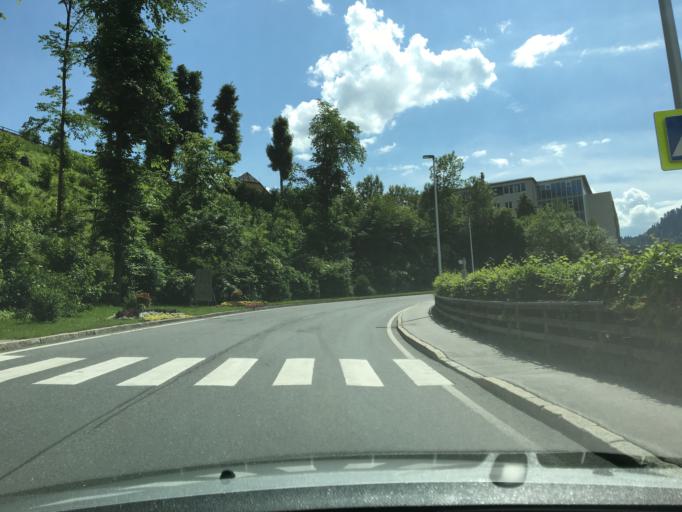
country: AT
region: Salzburg
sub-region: Politischer Bezirk Sankt Johann im Pongau
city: Sankt Johann im Pongau
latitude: 47.3525
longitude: 13.2069
